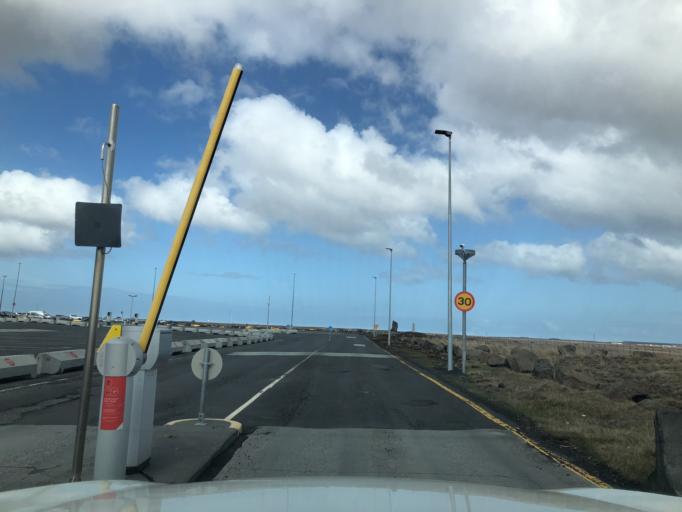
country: IS
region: Southern Peninsula
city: Reykjanesbaer
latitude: 63.9968
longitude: -22.6186
